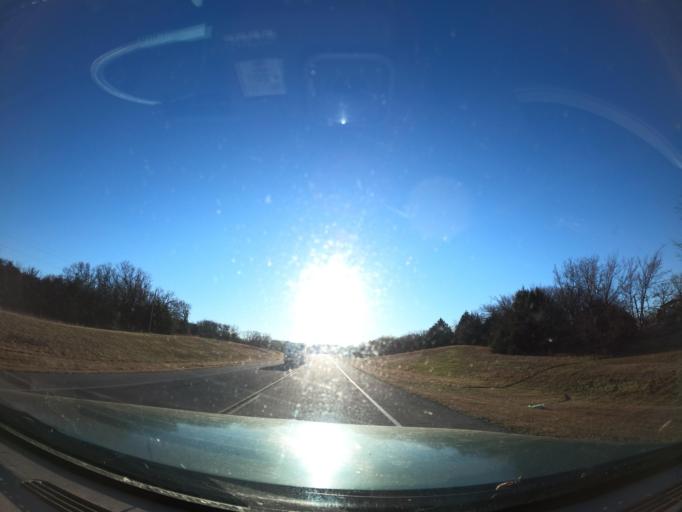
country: US
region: Oklahoma
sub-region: Pittsburg County
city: Hartshorne
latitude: 34.8666
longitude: -95.5222
